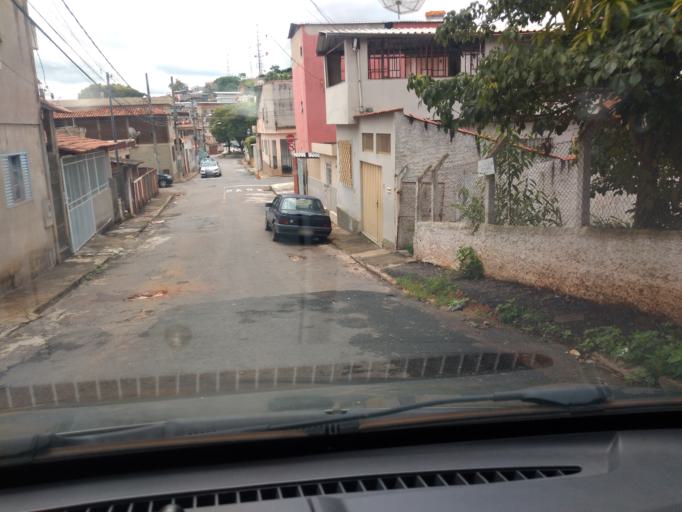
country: BR
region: Minas Gerais
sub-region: Tres Coracoes
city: Tres Coracoes
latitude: -21.6912
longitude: -45.2543
